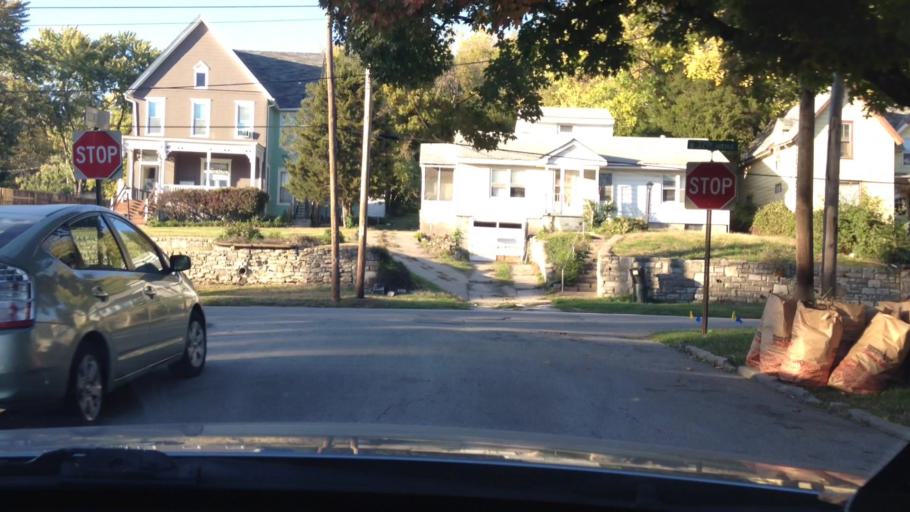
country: US
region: Kansas
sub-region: Johnson County
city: Roeland Park
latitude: 39.0603
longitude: -94.6300
